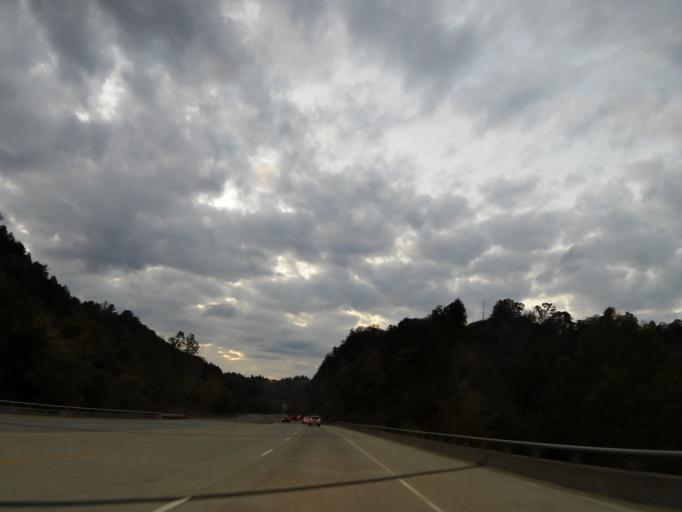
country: US
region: North Carolina
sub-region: Madison County
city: Marshall
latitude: 35.7687
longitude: -82.6182
